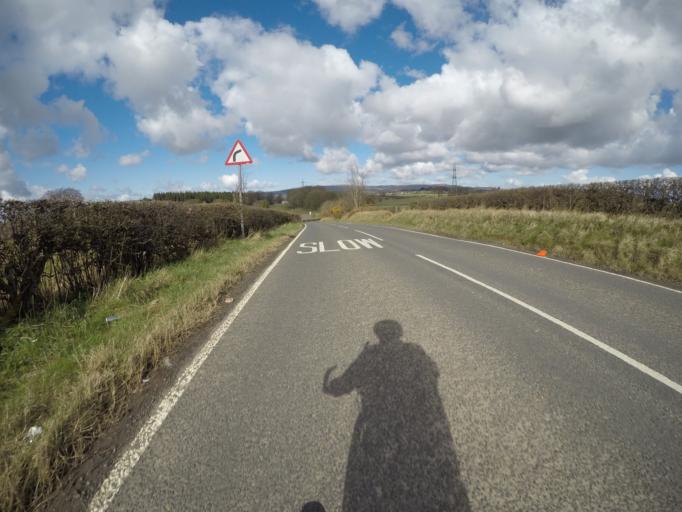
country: GB
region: Scotland
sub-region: North Ayrshire
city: Beith
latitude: 55.7389
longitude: -4.6227
